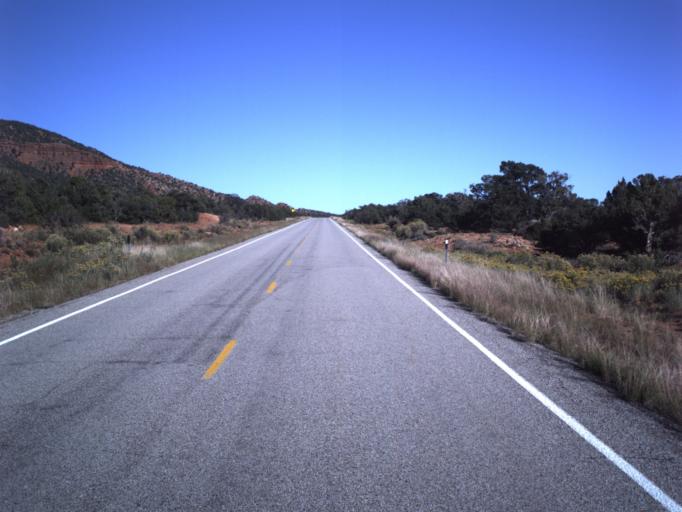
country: US
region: Utah
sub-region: San Juan County
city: Blanding
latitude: 37.5651
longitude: -109.8538
